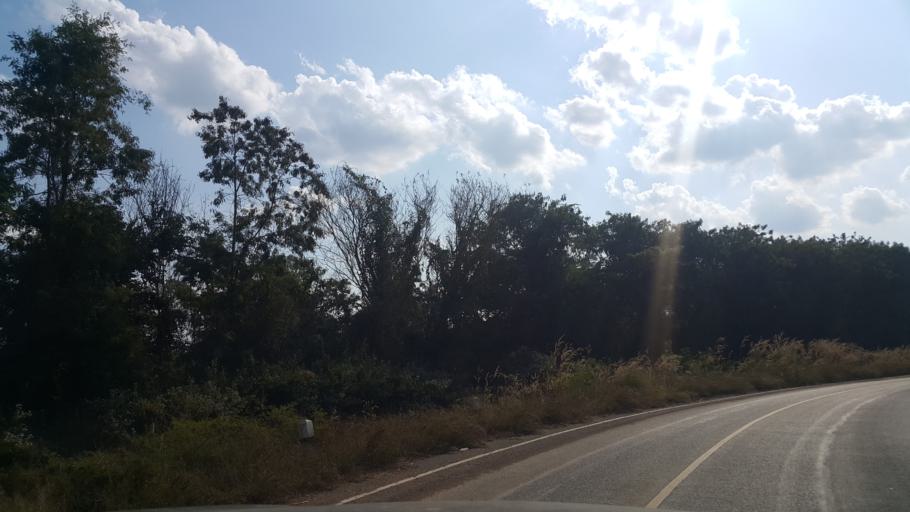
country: TH
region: Lamphun
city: Ban Thi
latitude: 18.5647
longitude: 99.1153
